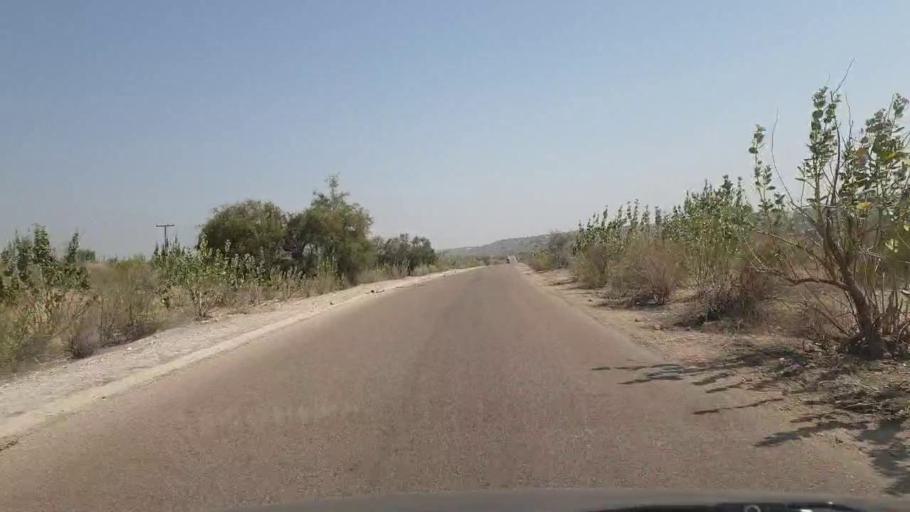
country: PK
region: Sindh
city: Chor
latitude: 25.6061
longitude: 70.0306
